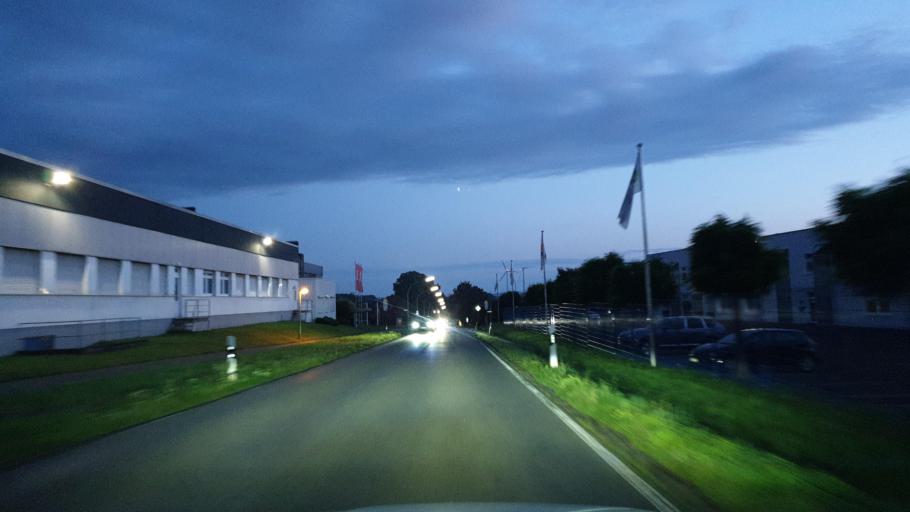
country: DE
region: North Rhine-Westphalia
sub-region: Regierungsbezirk Detmold
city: Huellhorst
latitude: 52.2588
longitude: 8.7021
